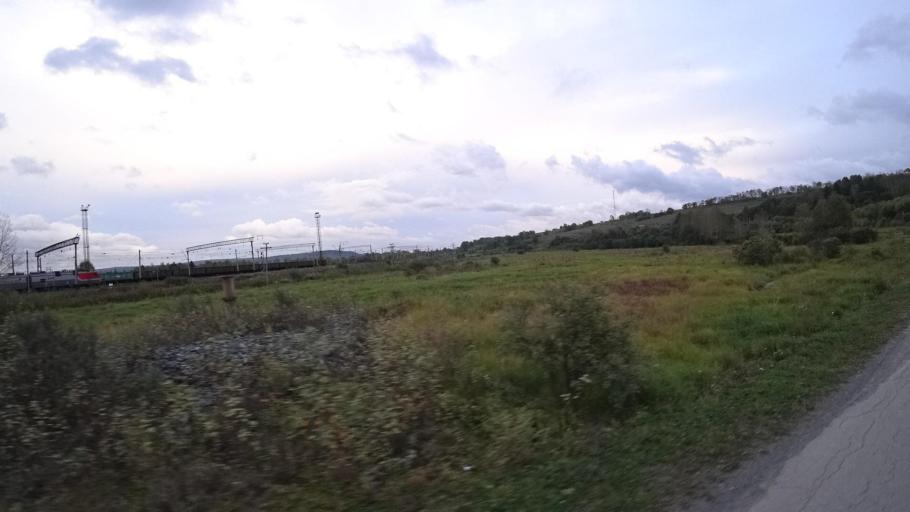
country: RU
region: Jewish Autonomous Oblast
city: Izvestkovyy
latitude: 48.9814
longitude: 131.5593
